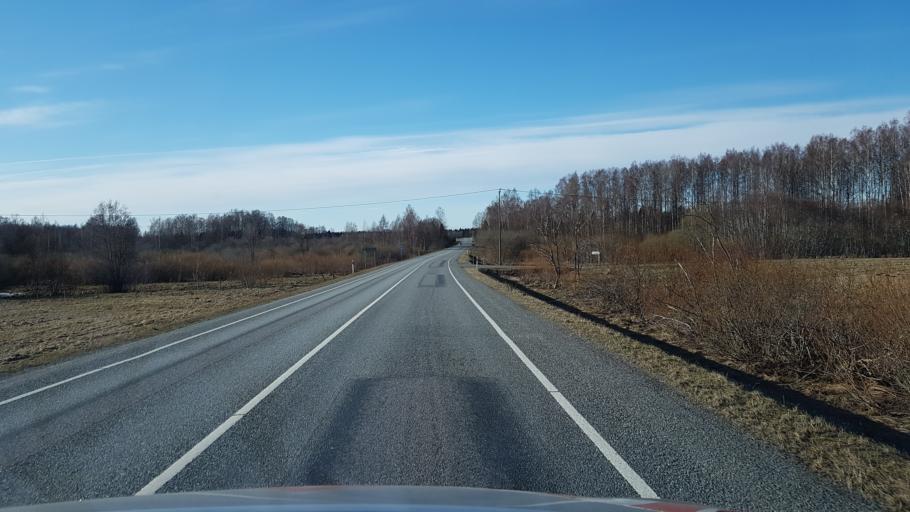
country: EE
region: Laeaene-Virumaa
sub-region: Tapa vald
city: Tapa
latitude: 59.4457
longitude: 25.9507
